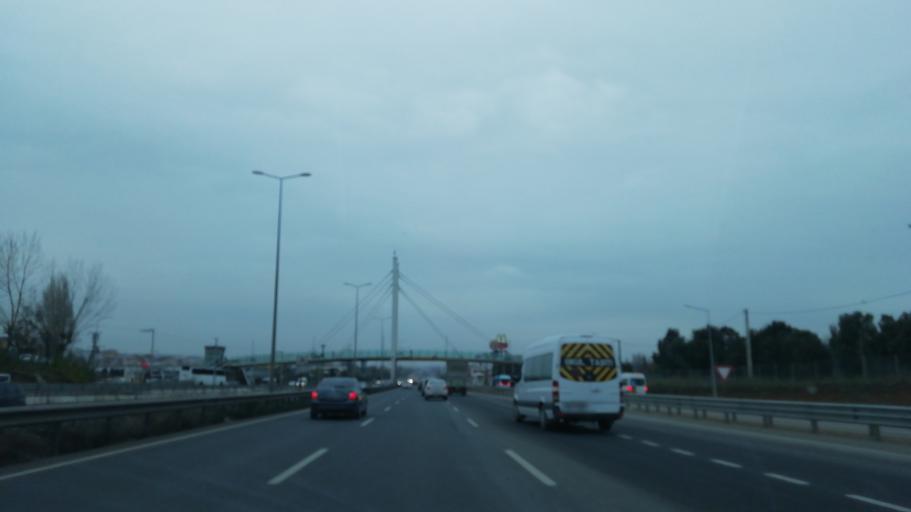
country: TR
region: Kocaeli
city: Darica
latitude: 40.8123
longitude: 29.3673
